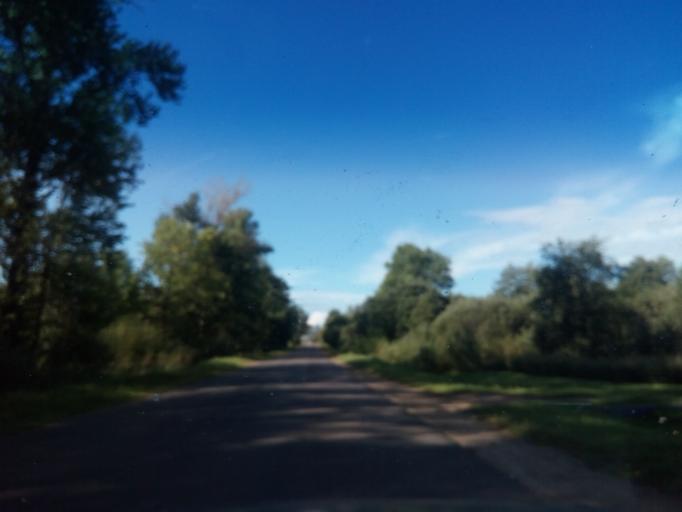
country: BY
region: Vitebsk
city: Dzisna
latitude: 55.6629
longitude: 28.3253
